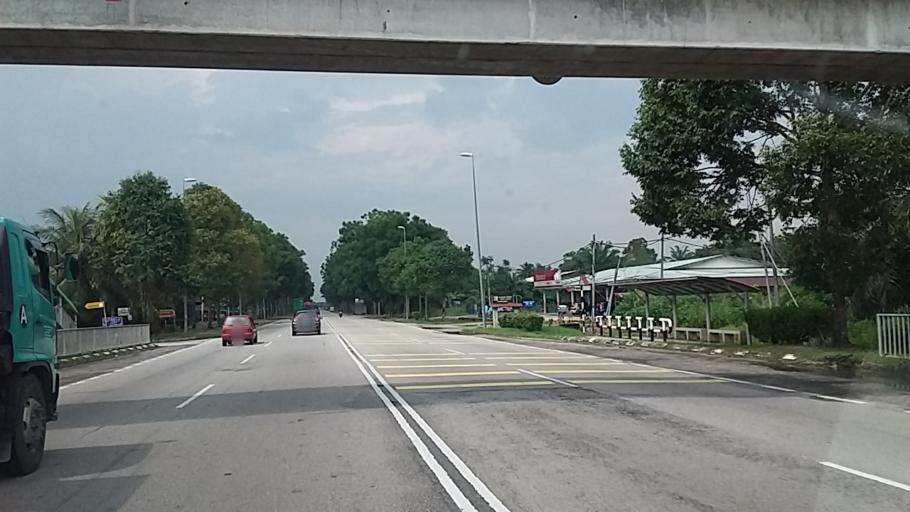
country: MY
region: Johor
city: Parit Raja
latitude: 1.8710
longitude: 103.1291
